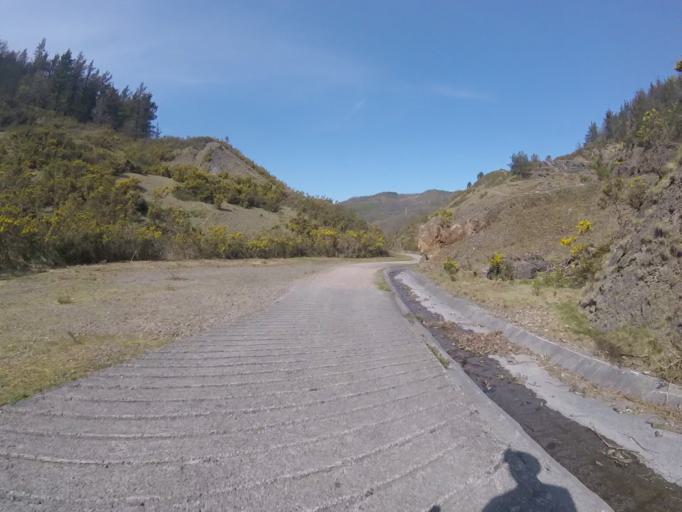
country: ES
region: Basque Country
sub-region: Provincia de Guipuzcoa
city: Irun
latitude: 43.2780
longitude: -1.8067
